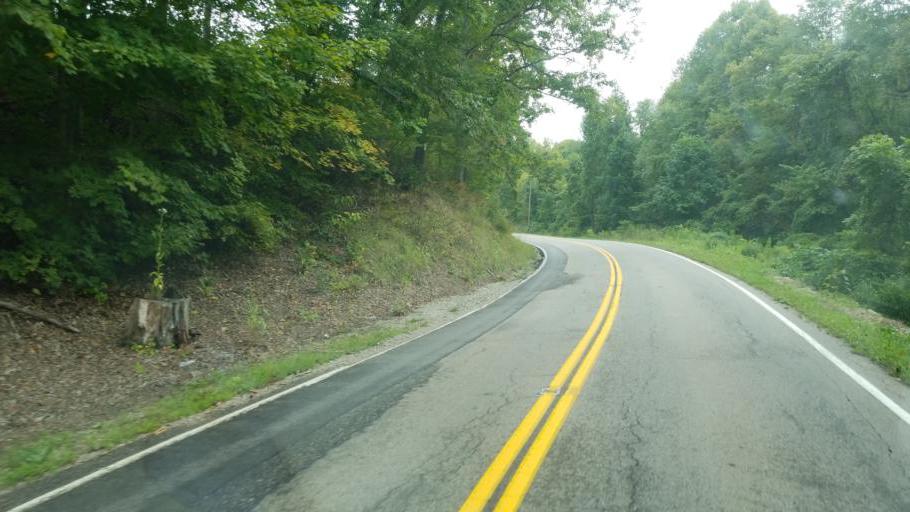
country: US
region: Ohio
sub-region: Jackson County
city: Oak Hill
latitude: 38.8856
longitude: -82.6797
